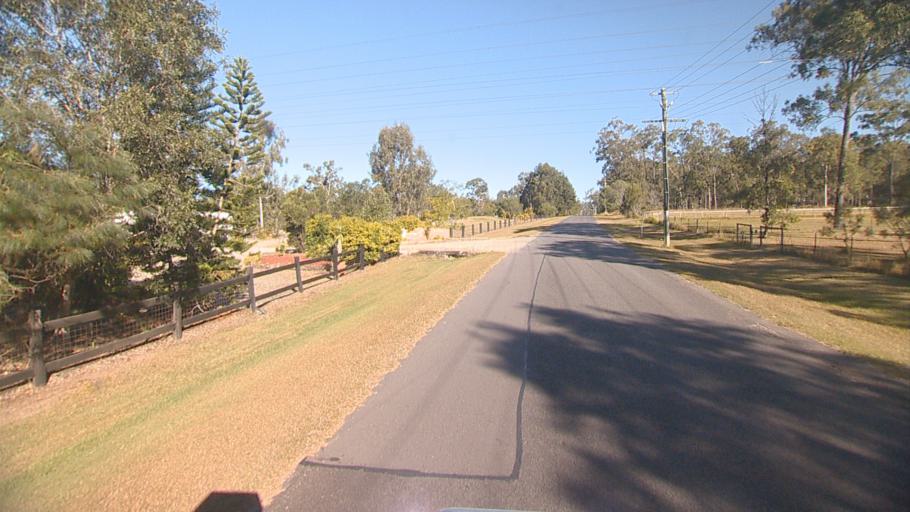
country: AU
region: Queensland
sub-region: Logan
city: Park Ridge South
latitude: -27.7327
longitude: 153.0220
